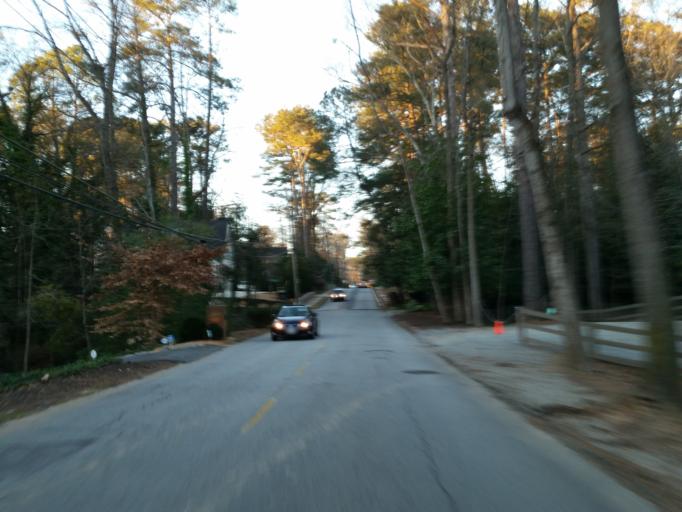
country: US
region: Georgia
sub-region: Cobb County
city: Vinings
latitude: 33.8239
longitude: -84.4293
